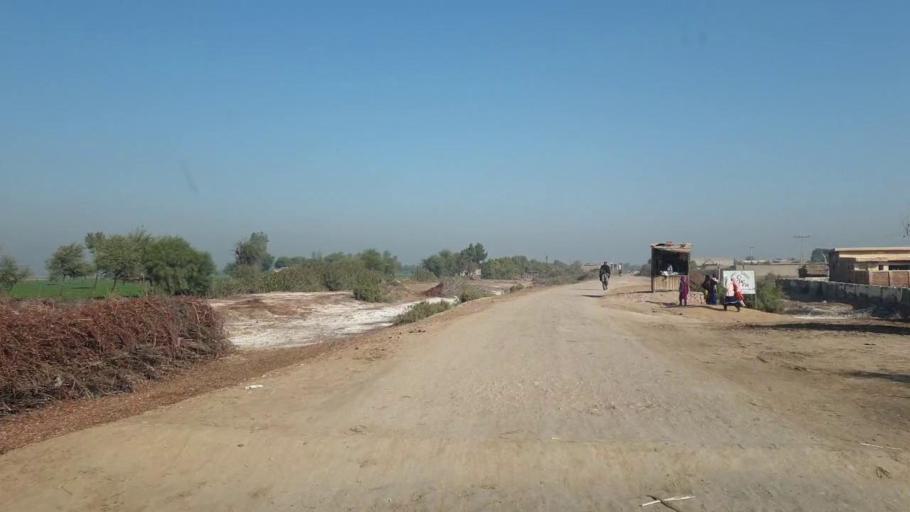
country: PK
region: Sindh
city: Bhit Shah
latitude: 25.9166
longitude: 68.5061
